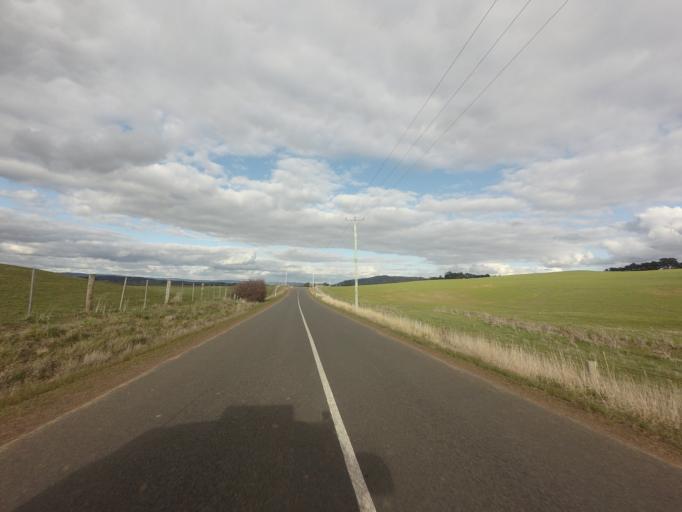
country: AU
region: Tasmania
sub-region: Northern Midlands
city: Evandale
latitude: -41.8928
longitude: 147.3350
